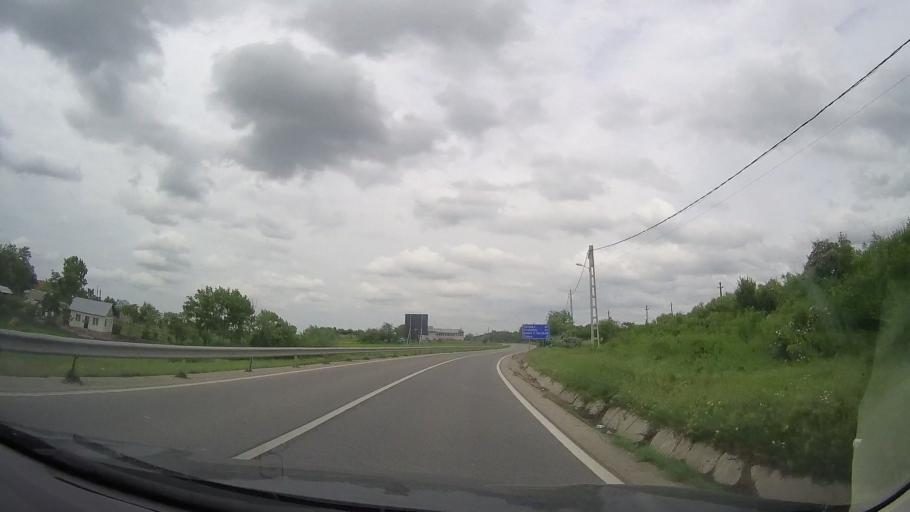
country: RO
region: Dolj
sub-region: Comuna Diosti
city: Radomir
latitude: 44.1235
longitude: 24.1586
